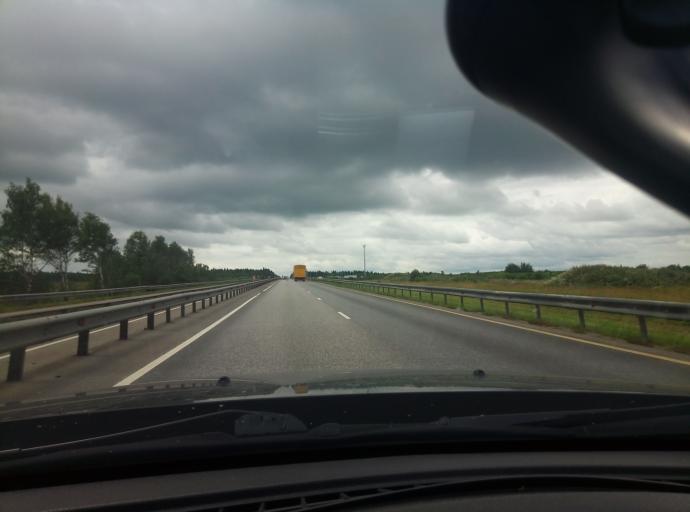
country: RU
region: Kaluga
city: Maloyaroslavets
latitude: 55.0120
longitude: 36.5471
